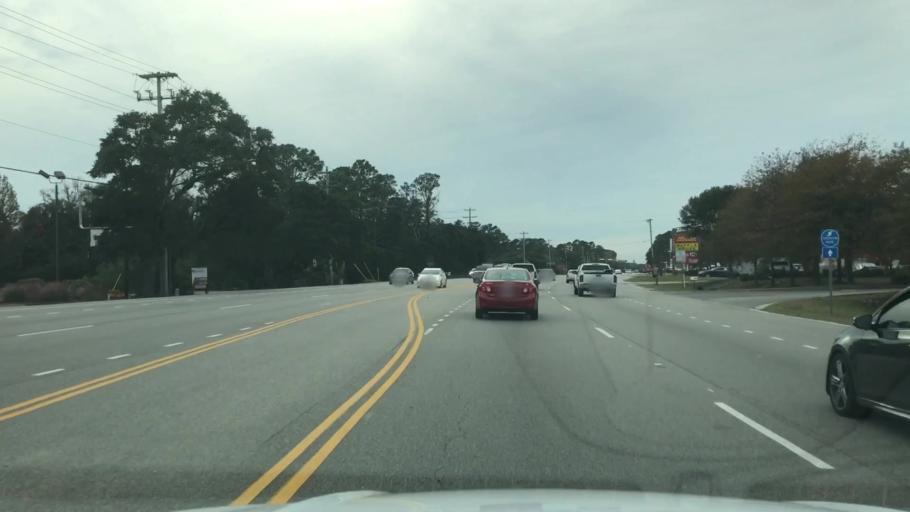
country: US
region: South Carolina
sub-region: Georgetown County
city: Murrells Inlet
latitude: 33.4381
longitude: -79.1283
